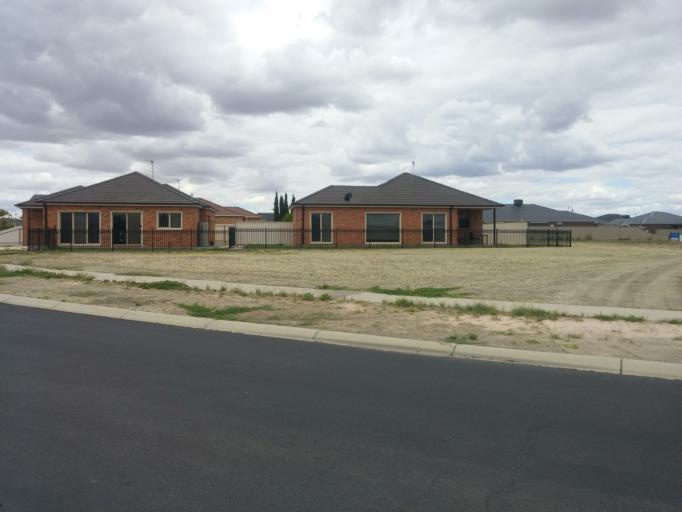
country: AU
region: Victoria
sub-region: Horsham
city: Horsham
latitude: -36.7276
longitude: 142.1992
